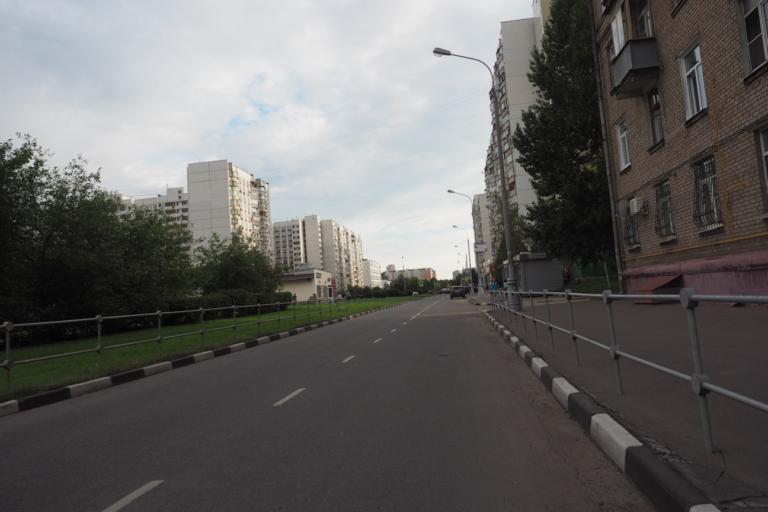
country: RU
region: Moscow
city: Novyye Cheremushki
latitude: 55.6846
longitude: 37.5815
